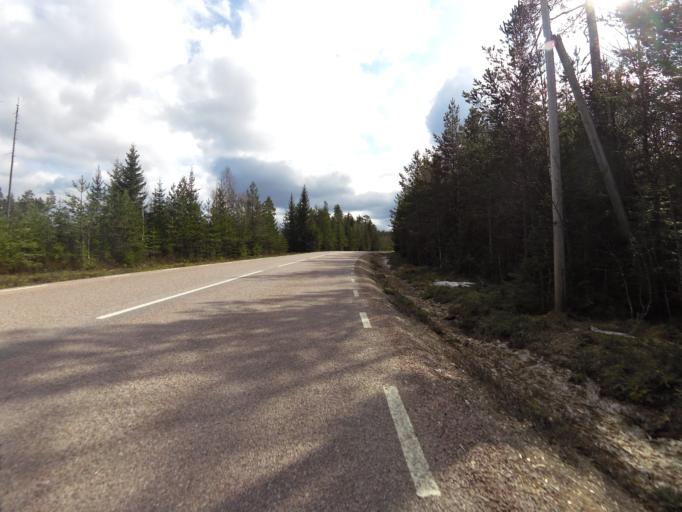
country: SE
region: Dalarna
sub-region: Avesta Kommun
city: Horndal
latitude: 60.3021
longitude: 16.2674
